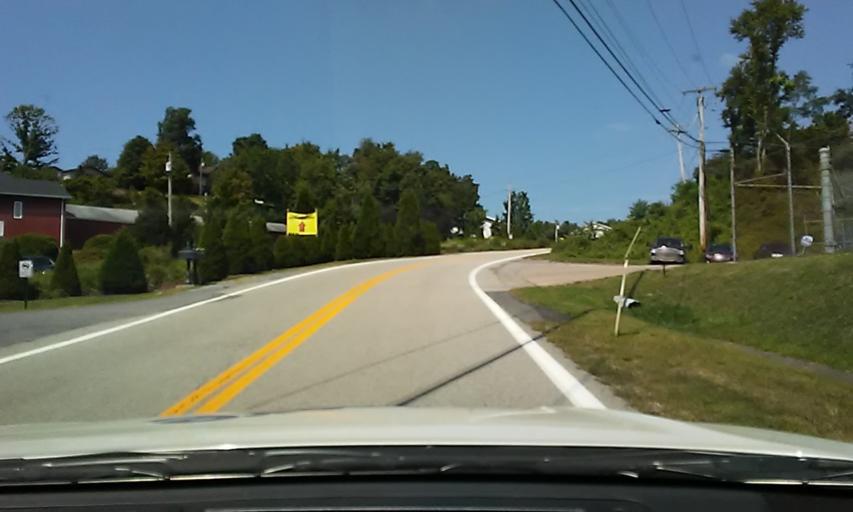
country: US
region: West Virginia
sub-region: Monongalia County
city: Westover
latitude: 39.6279
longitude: -79.9919
